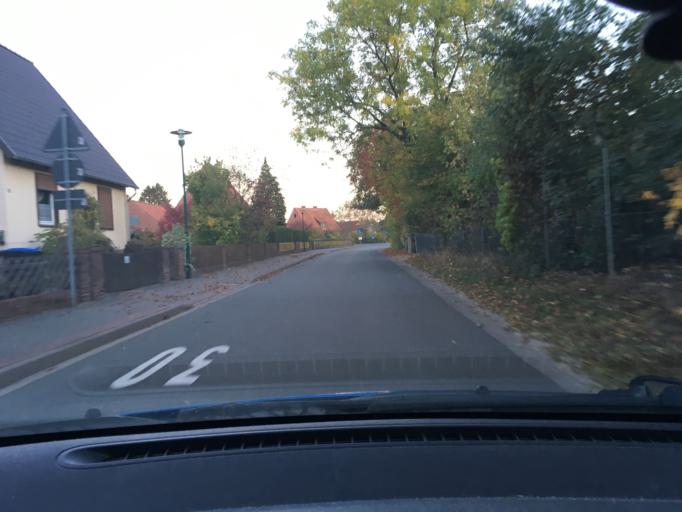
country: DE
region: Lower Saxony
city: Neetze
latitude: 53.2733
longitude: 10.6202
